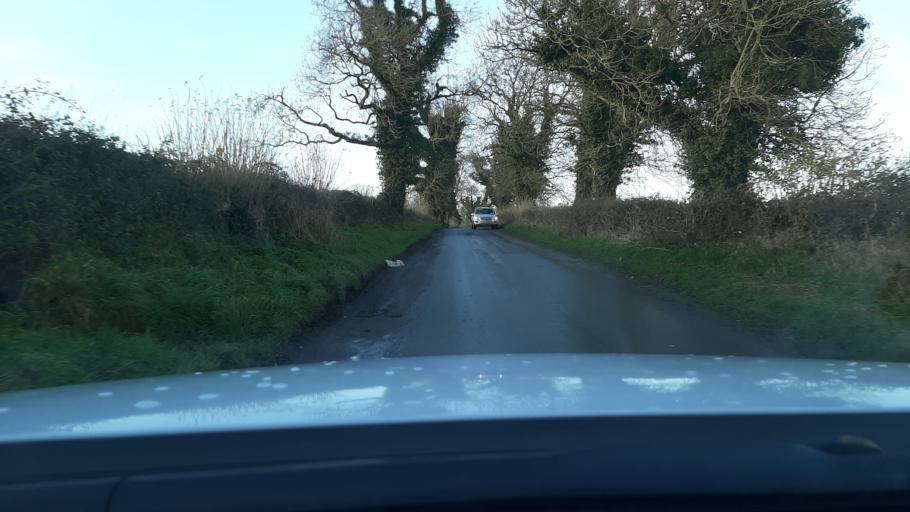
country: IE
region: Leinster
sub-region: Kildare
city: Kildare
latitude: 53.1661
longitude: -6.9224
